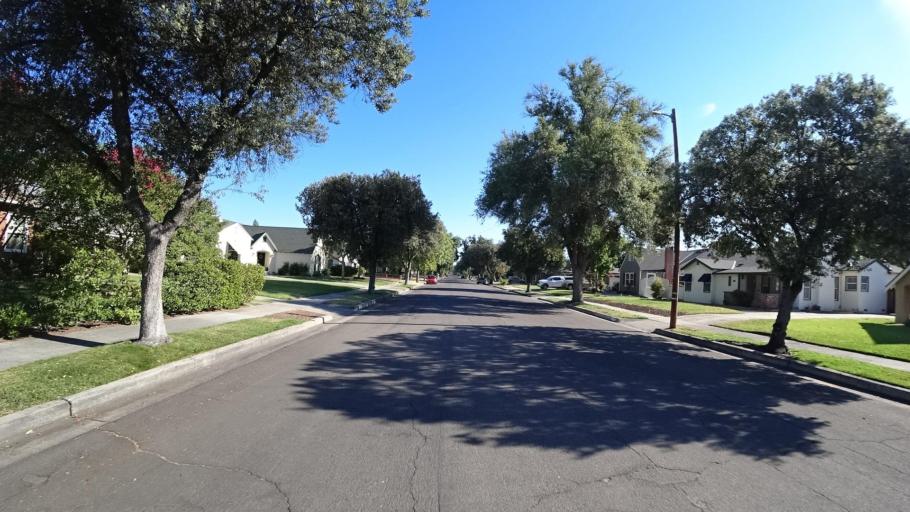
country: US
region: California
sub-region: Fresno County
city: Fresno
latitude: 36.7617
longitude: -119.8132
